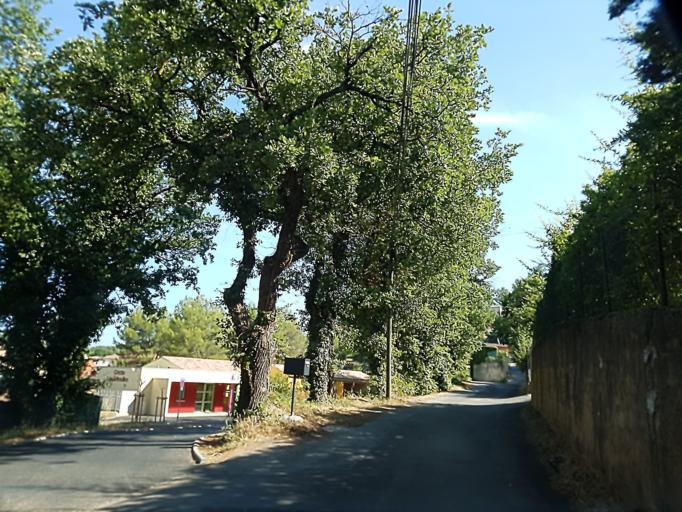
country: FR
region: Provence-Alpes-Cote d'Azur
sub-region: Departement du Var
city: Bras
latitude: 43.4695
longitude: 5.9580
